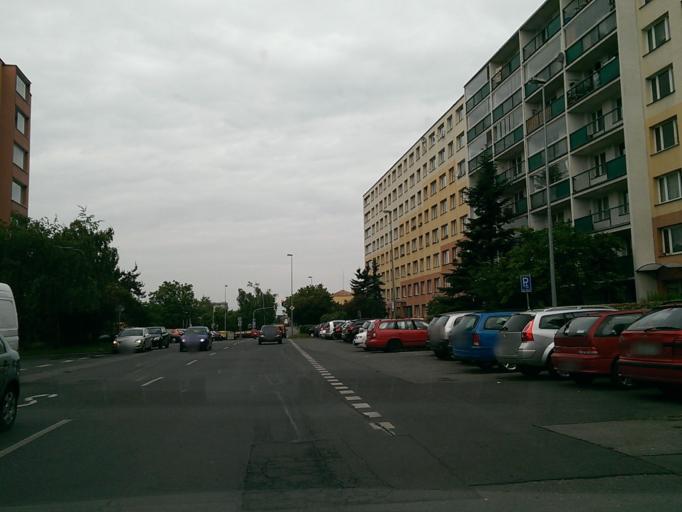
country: CZ
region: Praha
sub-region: Praha 8
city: Liben
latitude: 50.0566
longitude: 14.4957
